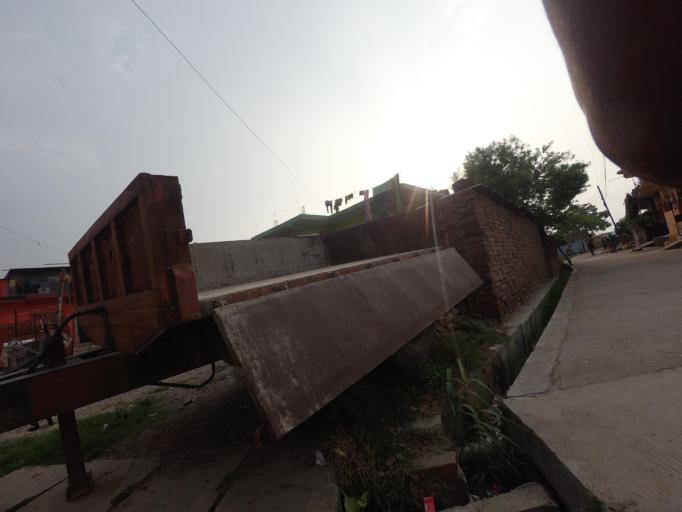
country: NP
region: Western Region
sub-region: Lumbini Zone
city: Bhairahawa
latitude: 27.5048
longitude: 83.4414
